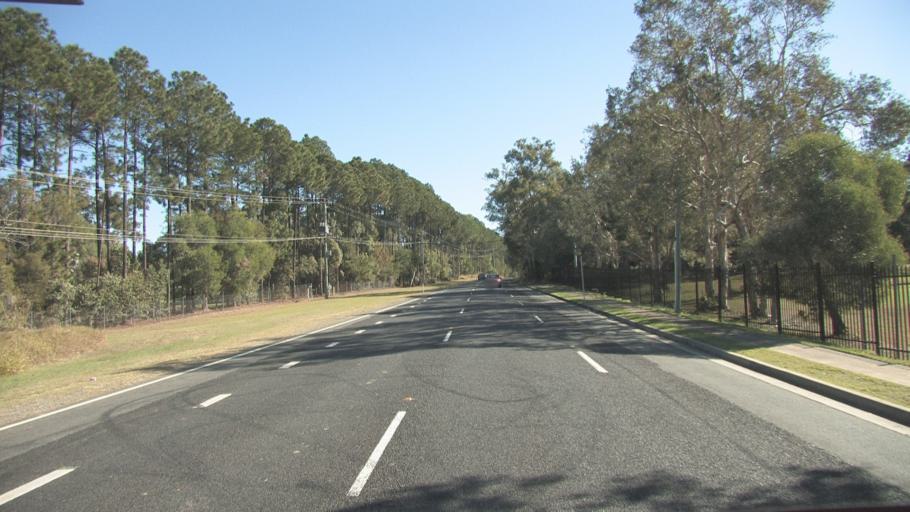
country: AU
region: Queensland
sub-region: Logan
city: Logan Reserve
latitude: -27.7210
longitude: 153.0841
